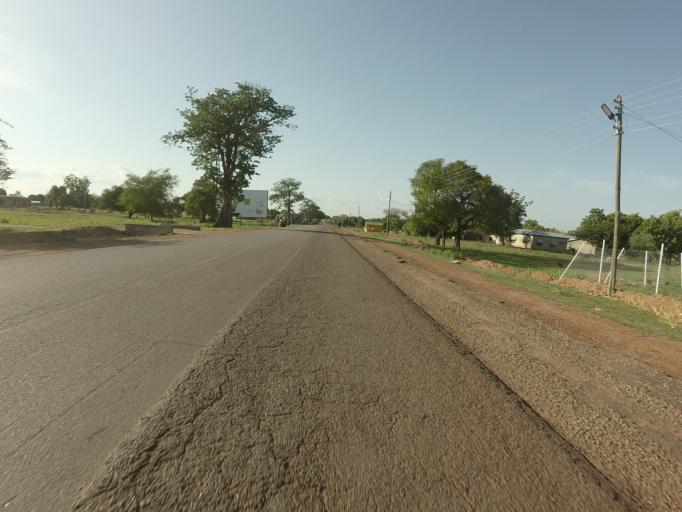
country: GH
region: Upper East
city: Navrongo
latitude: 10.9111
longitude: -1.0902
